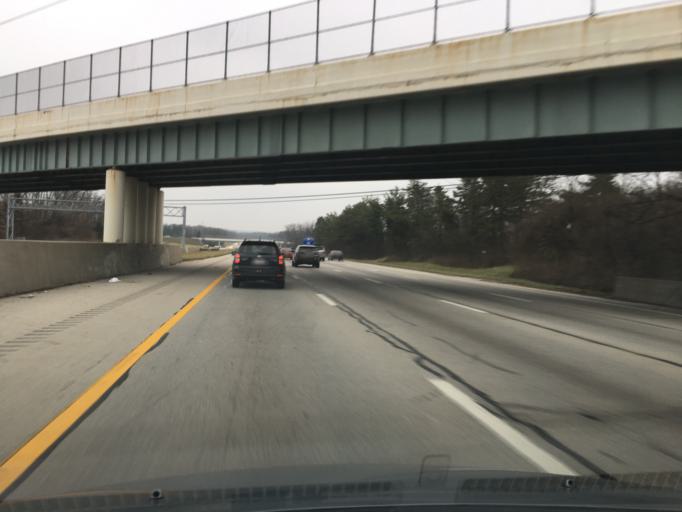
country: US
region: Ohio
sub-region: Hamilton County
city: Sixteen Mile Stand
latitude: 39.2650
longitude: -84.3431
